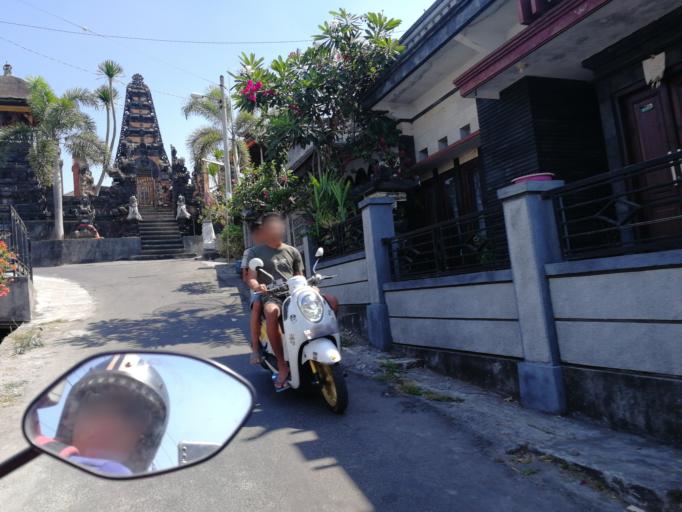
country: ID
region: Bali
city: Banjar Kedisan
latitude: -8.1495
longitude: 115.3063
